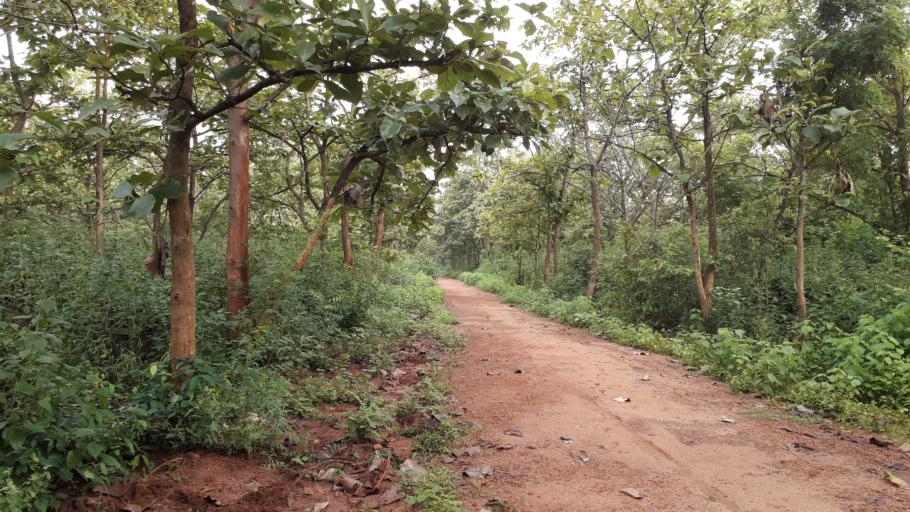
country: IN
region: Andhra Pradesh
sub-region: East Godavari
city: Rajahmundry
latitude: 17.0346
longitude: 81.8215
